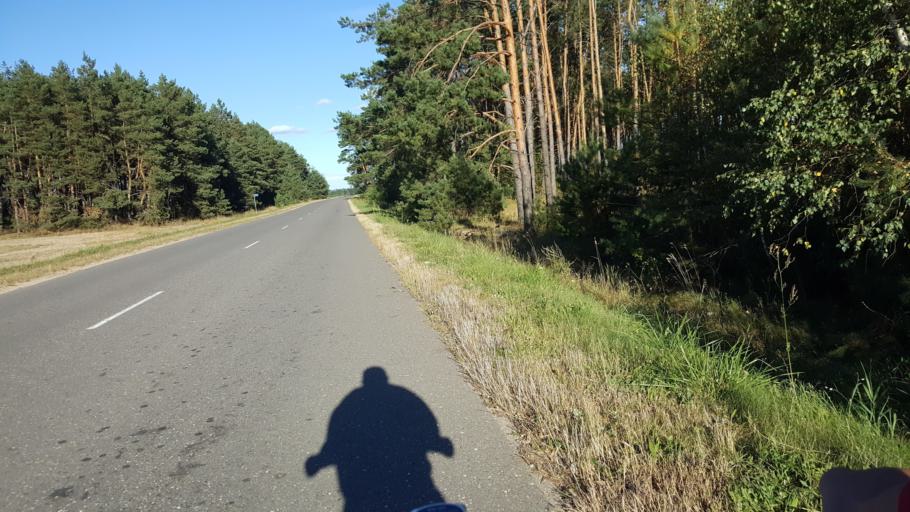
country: BY
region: Brest
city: Kamyanyets
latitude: 52.3888
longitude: 23.7378
